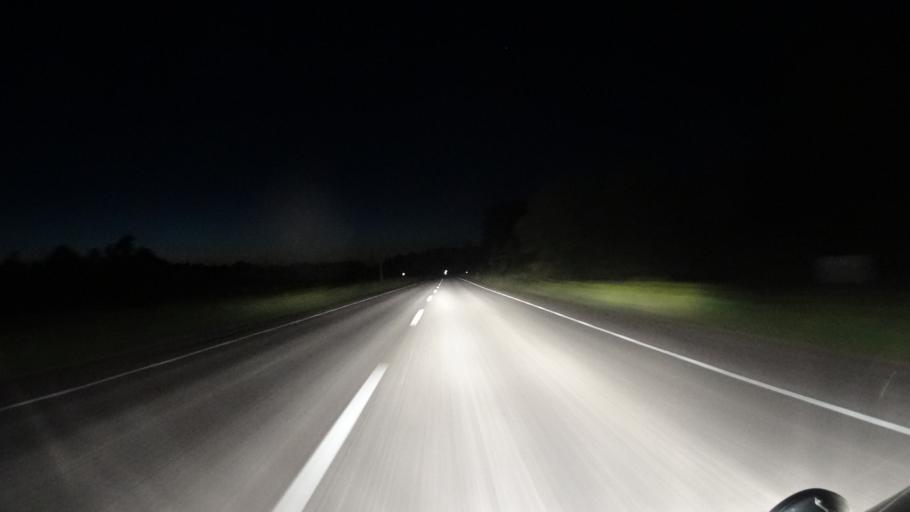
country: SE
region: OEstergoetland
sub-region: Odeshogs Kommun
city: OEdeshoeg
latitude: 58.2743
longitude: 14.7550
